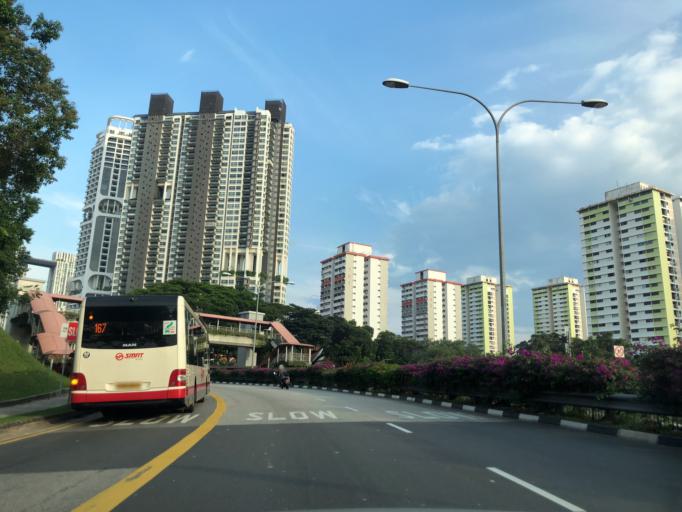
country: SG
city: Singapore
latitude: 1.2763
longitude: 103.8342
